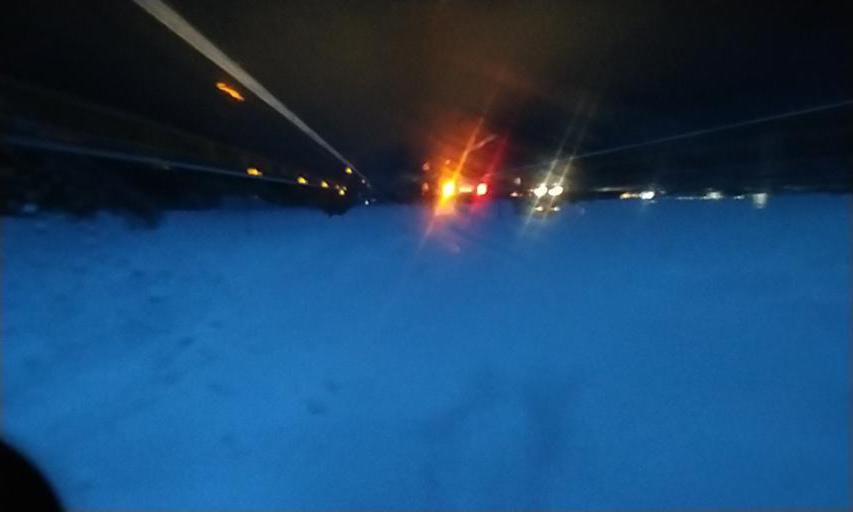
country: ES
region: Extremadura
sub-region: Provincia de Caceres
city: Aldea del Cano
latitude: 39.3722
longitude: -6.3418
